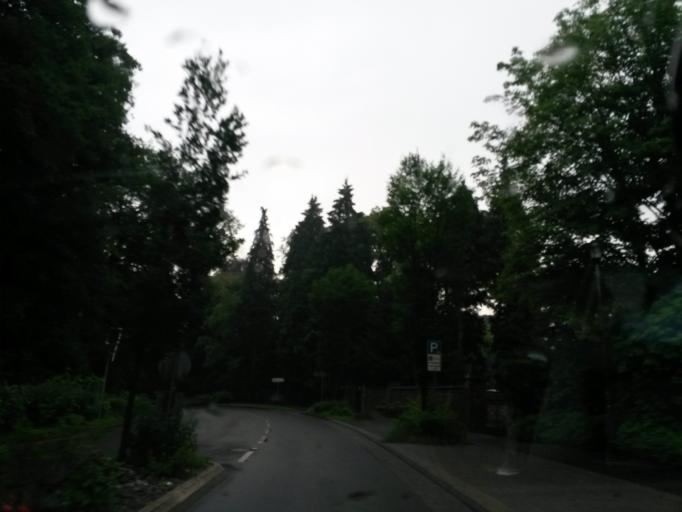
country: DE
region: North Rhine-Westphalia
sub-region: Regierungsbezirk Koln
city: Engelskirchen
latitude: 50.9835
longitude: 7.4104
